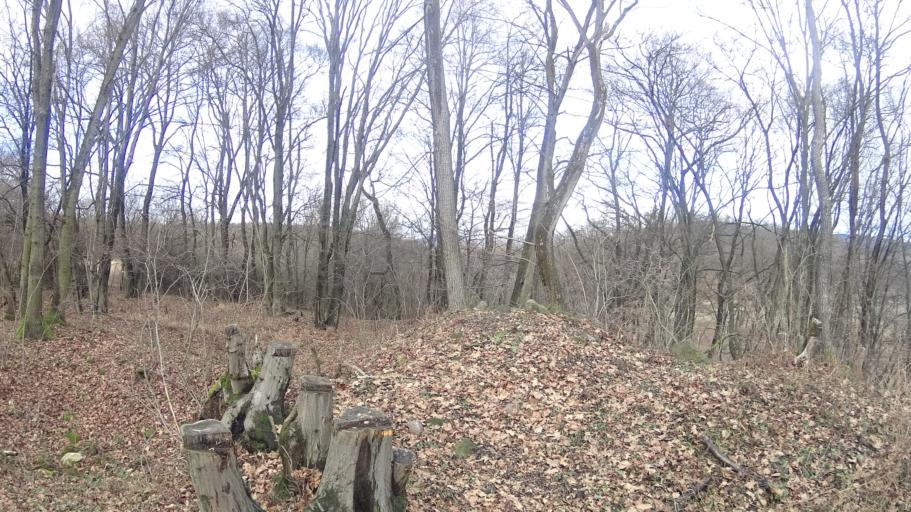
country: HU
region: Pest
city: Nagymaros
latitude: 47.8485
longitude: 18.9439
